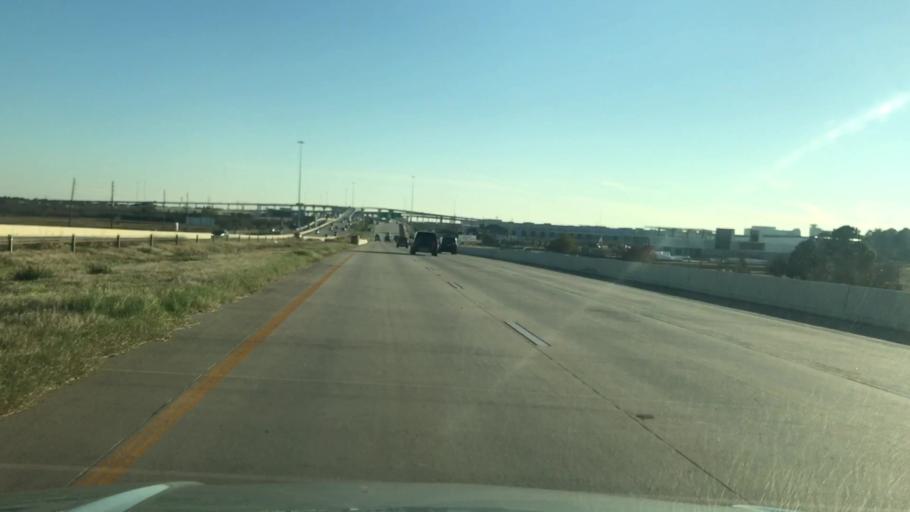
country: US
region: Texas
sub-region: Harris County
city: Katy
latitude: 29.8008
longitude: -95.7757
